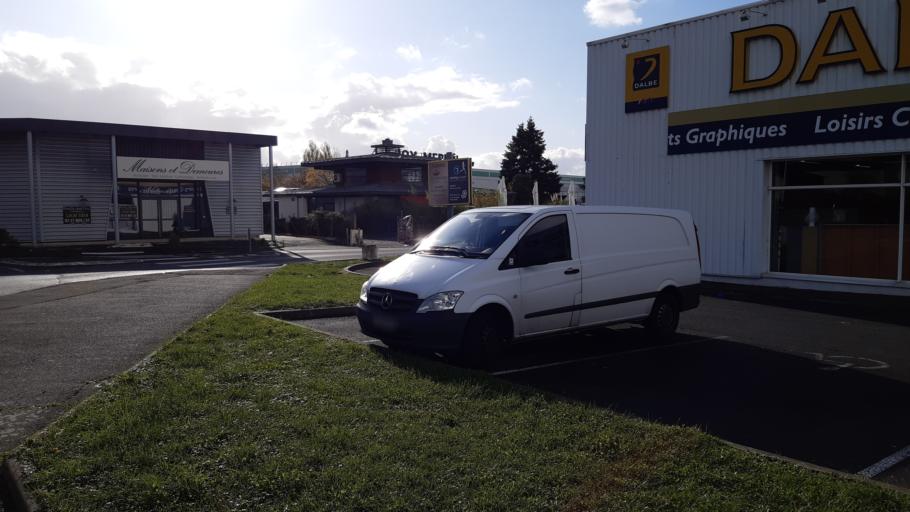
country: FR
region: Centre
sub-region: Departement d'Indre-et-Loire
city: Chanceaux-sur-Choisille
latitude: 47.4259
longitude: 0.7050
